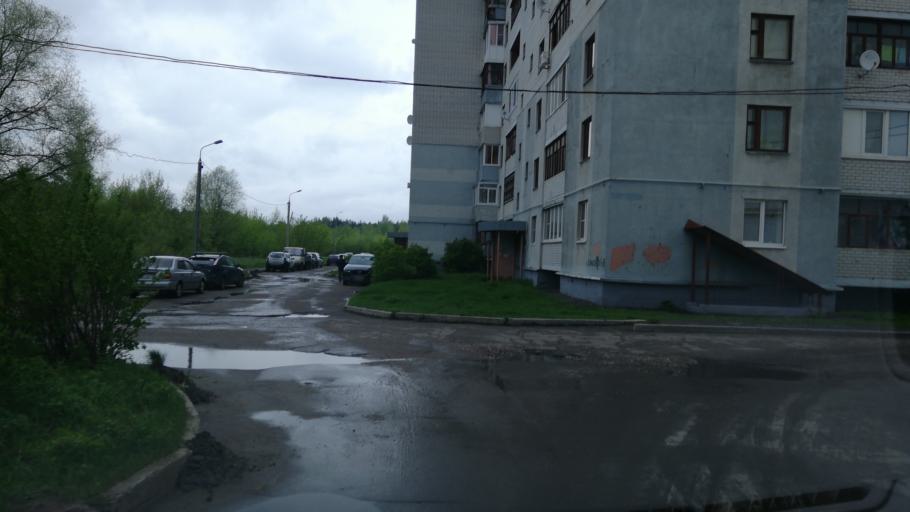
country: RU
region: Jaroslavl
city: Yaroslavl
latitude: 57.6578
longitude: 39.9244
